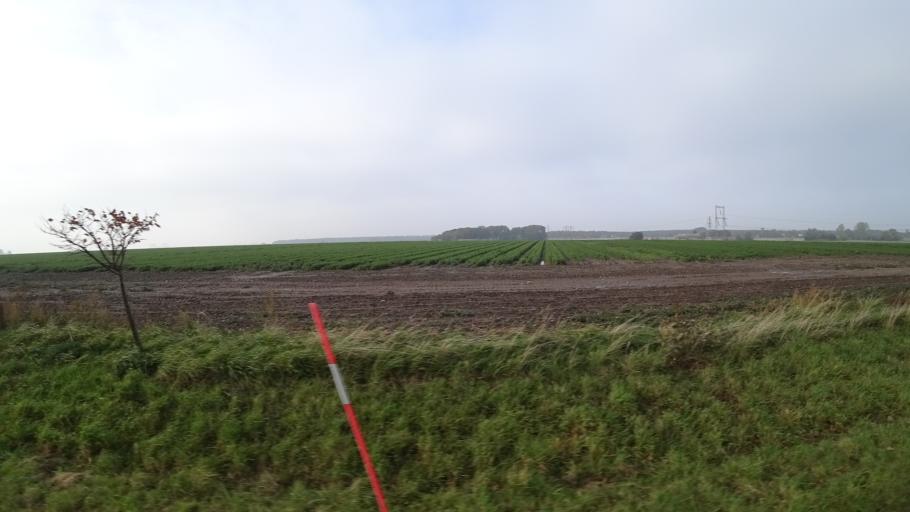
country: SE
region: Skane
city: Bjarred
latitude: 55.7406
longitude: 12.9909
